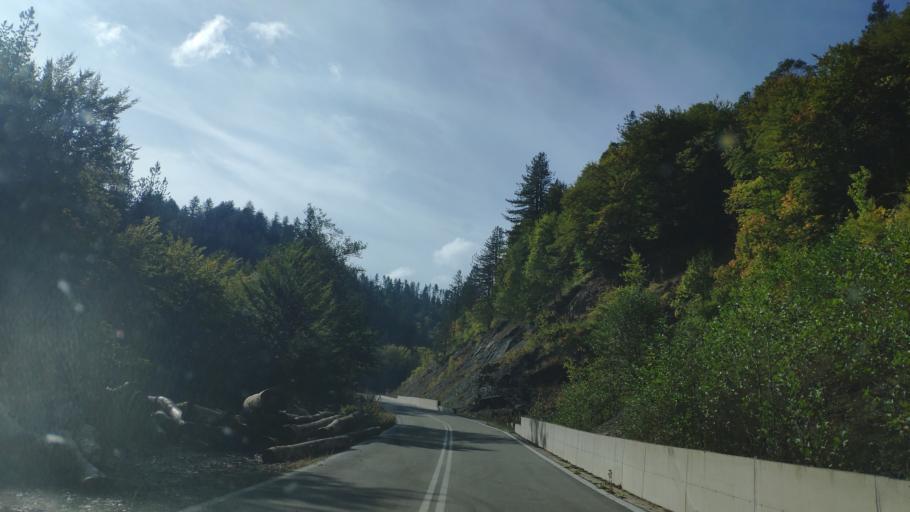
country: GR
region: West Macedonia
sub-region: Nomos Kastorias
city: Nestorio
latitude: 40.3789
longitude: 20.9411
